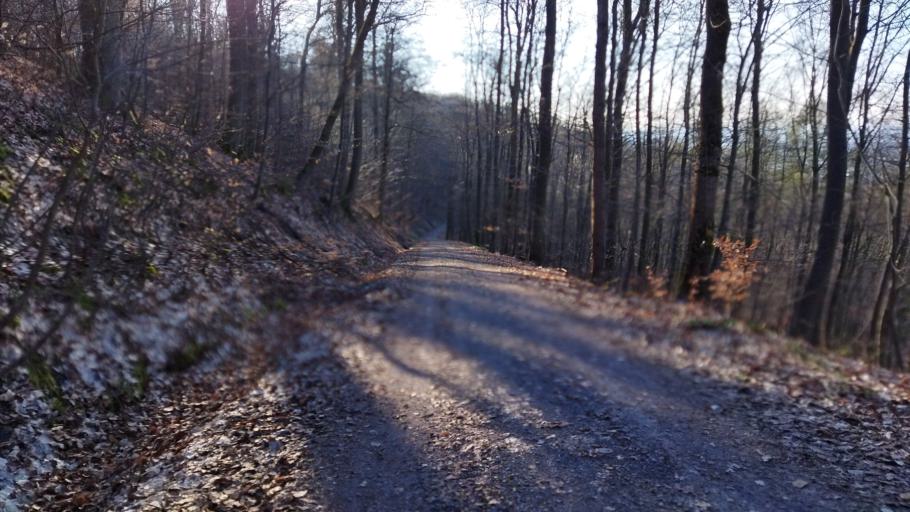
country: DE
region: Baden-Wuerttemberg
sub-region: Karlsruhe Region
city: Sternenfels
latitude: 49.0471
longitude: 8.8646
